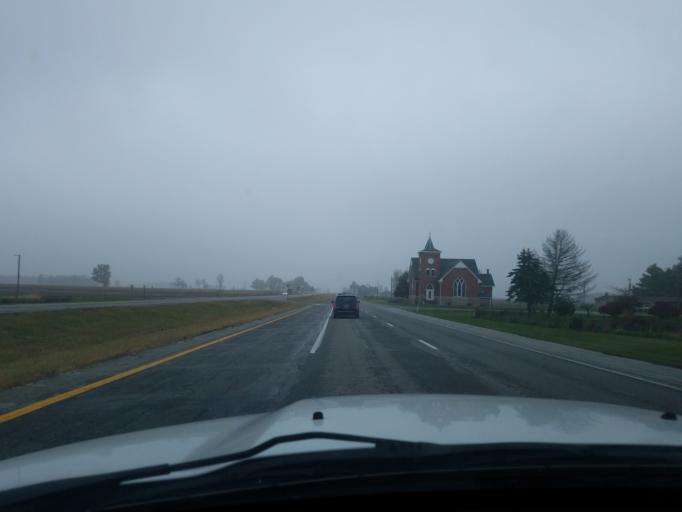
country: US
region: Indiana
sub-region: Tipton County
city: Tipton
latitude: 40.3165
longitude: -86.1269
